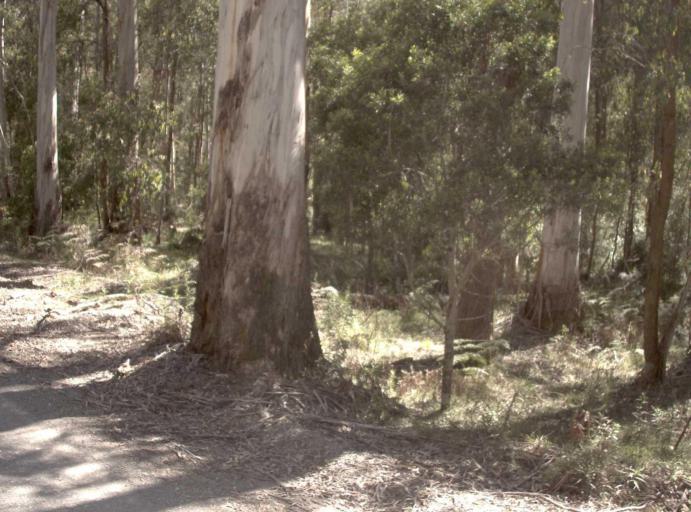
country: AU
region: New South Wales
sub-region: Bombala
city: Bombala
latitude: -37.2059
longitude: 148.7313
